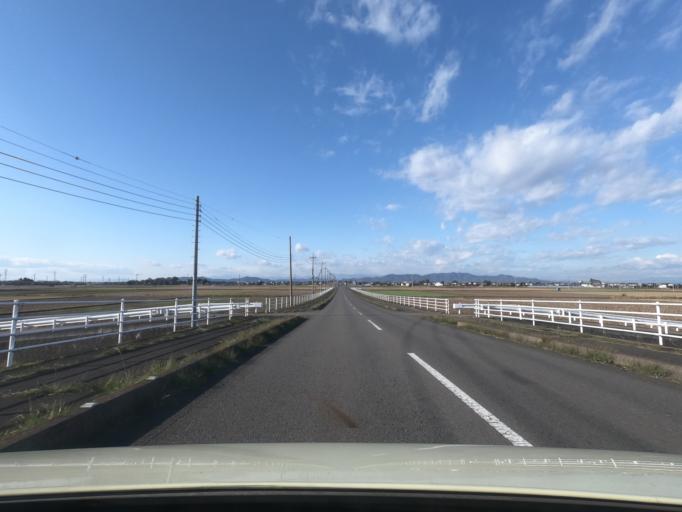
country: JP
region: Tochigi
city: Fujioka
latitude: 36.2627
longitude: 139.7221
